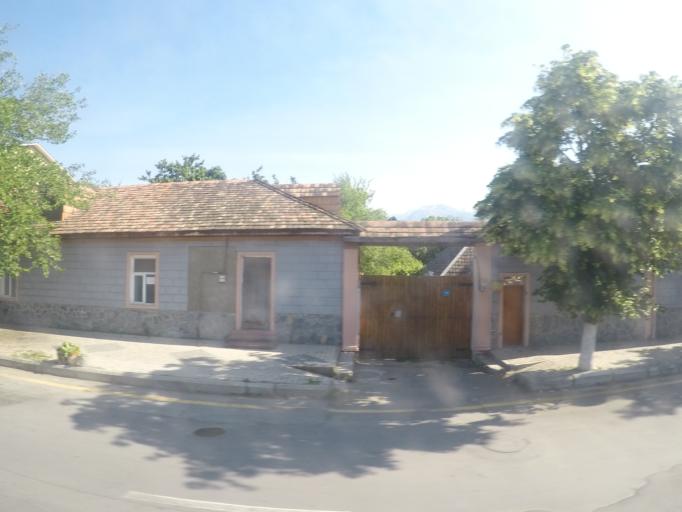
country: AZ
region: Shaki City
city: Sheki
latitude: 41.2015
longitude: 47.1751
